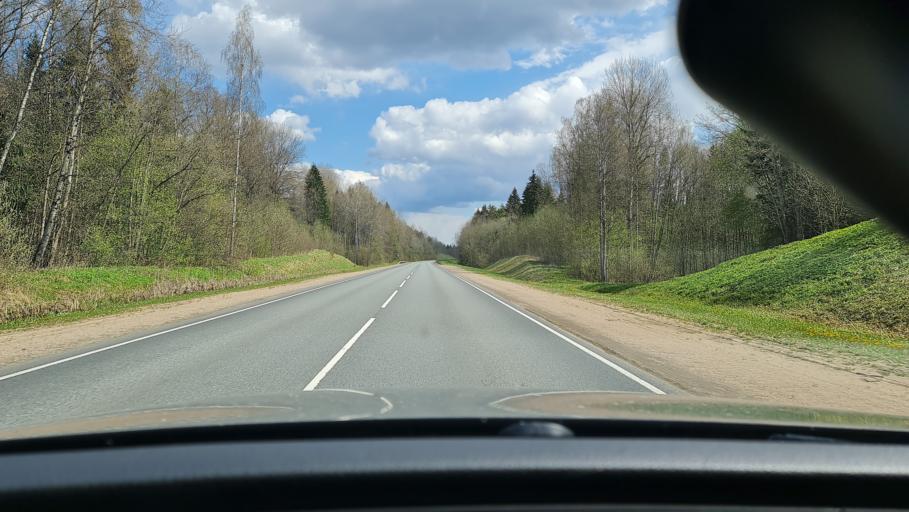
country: RU
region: Tverskaya
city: Zapadnaya Dvina
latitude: 56.3328
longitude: 31.8932
